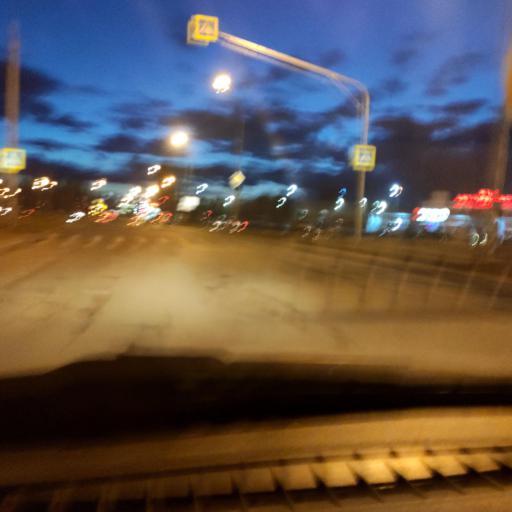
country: RU
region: Samara
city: Tol'yatti
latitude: 53.5437
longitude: 49.3181
